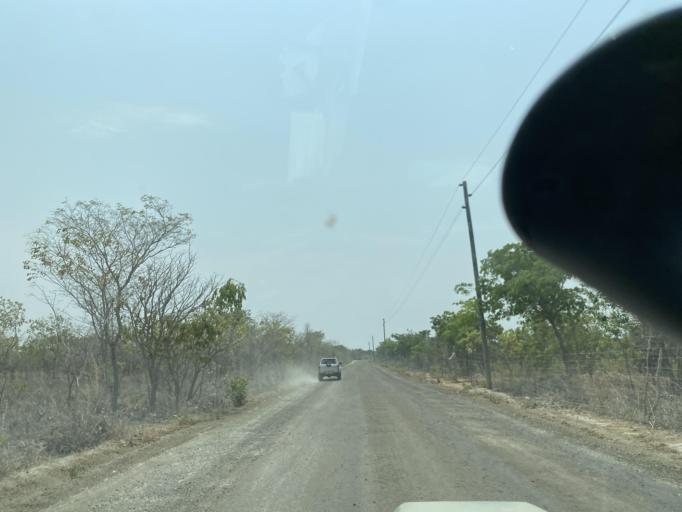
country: ZM
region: Lusaka
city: Lusaka
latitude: -15.5282
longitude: 28.4454
